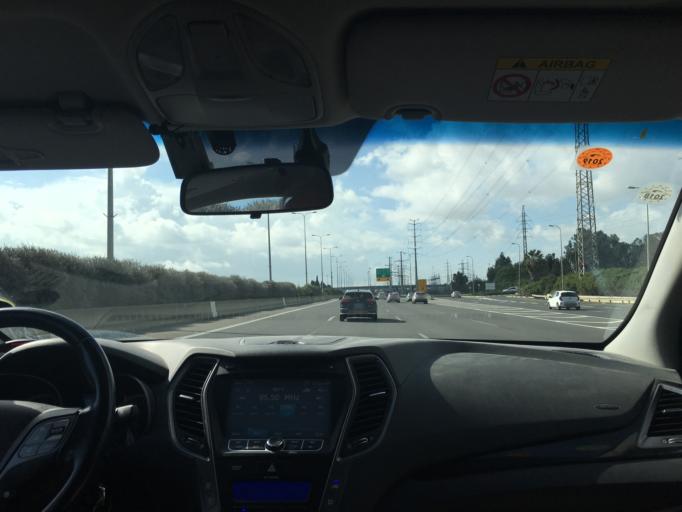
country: IL
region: Tel Aviv
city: Azor
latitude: 32.0267
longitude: 34.8271
